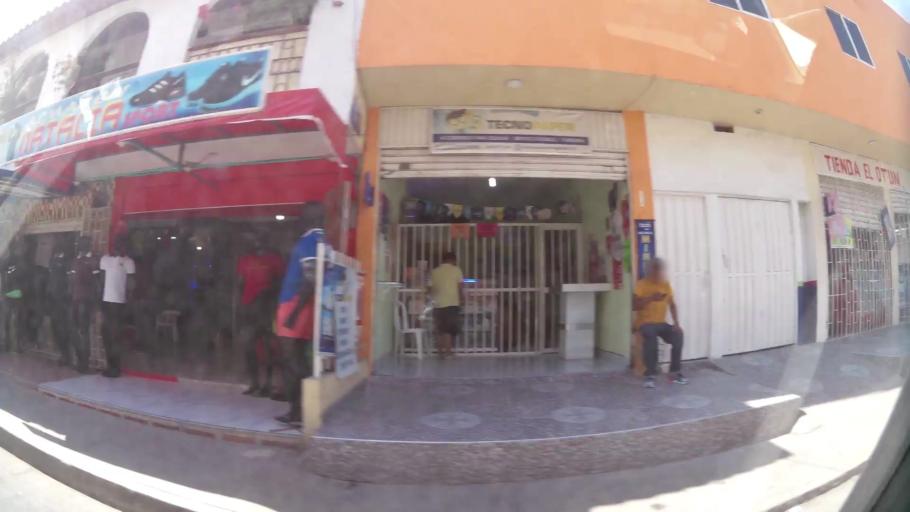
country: CO
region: Bolivar
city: Cartagena
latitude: 10.3866
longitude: -75.4587
